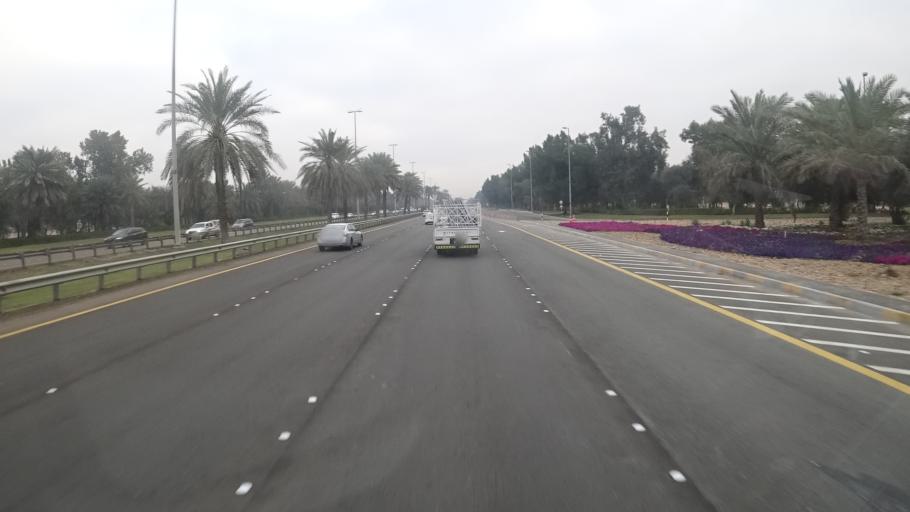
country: AE
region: Abu Dhabi
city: Abu Dhabi
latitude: 24.4015
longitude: 54.5945
